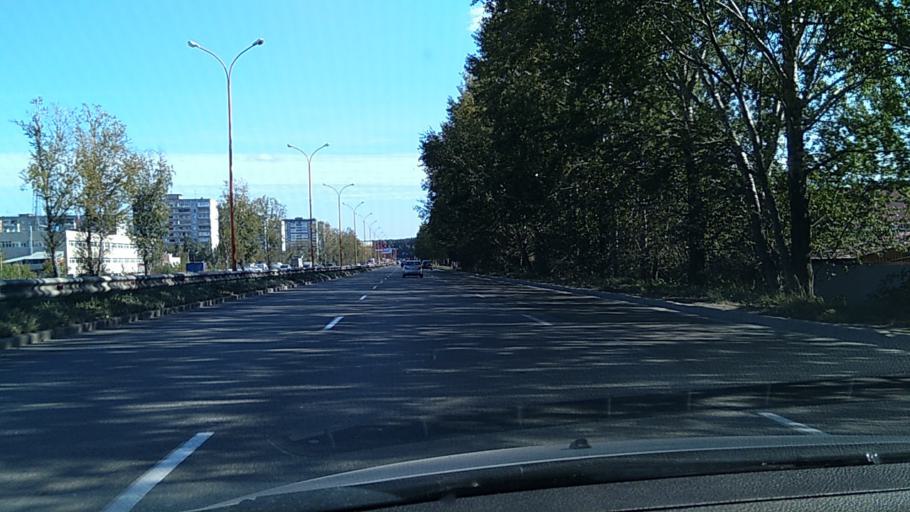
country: RU
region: Sverdlovsk
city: Sovkhoznyy
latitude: 56.7954
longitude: 60.5629
